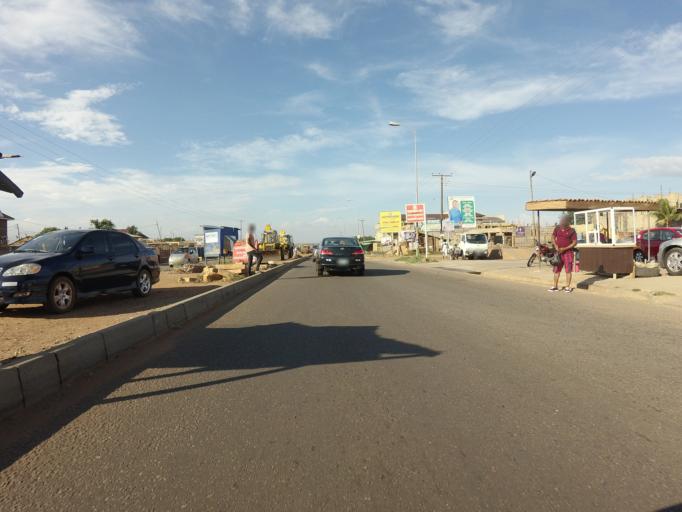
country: GH
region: Greater Accra
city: Nungua
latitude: 5.6438
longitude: -0.0598
